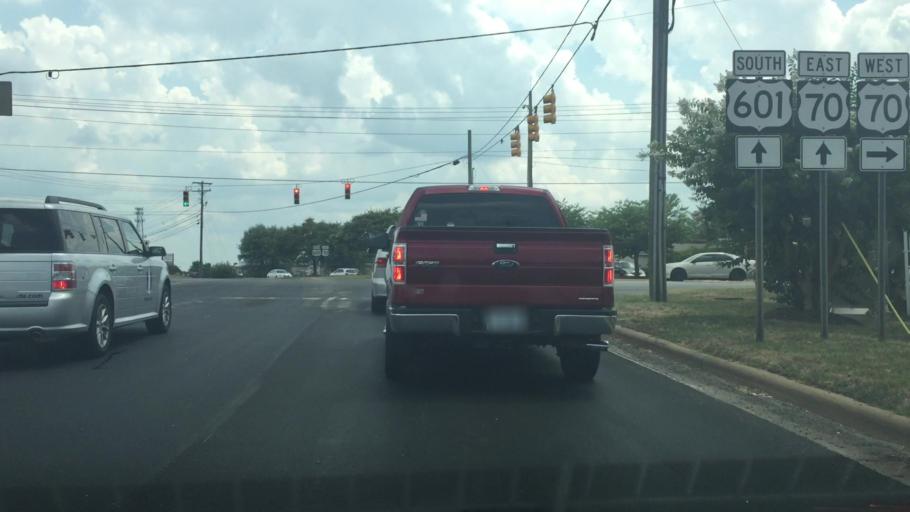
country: US
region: North Carolina
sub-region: Rowan County
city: Franklin
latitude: 35.6942
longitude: -80.5128
